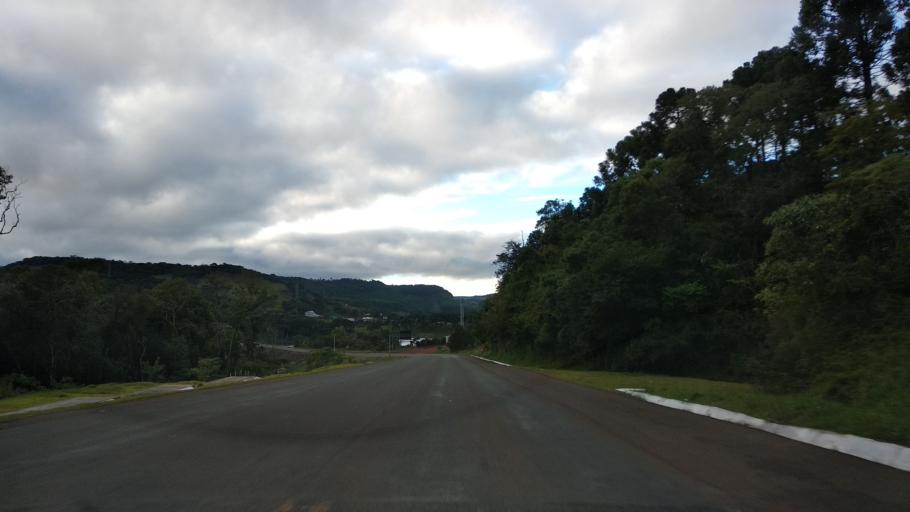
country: BR
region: Santa Catarina
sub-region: Curitibanos
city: Curitibanos
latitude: -27.5359
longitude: -50.8683
